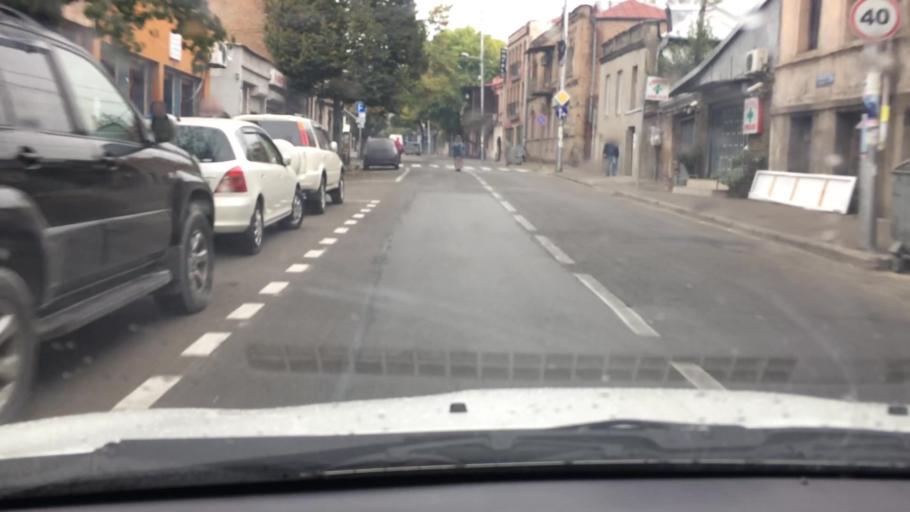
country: GE
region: T'bilisi
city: Tbilisi
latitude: 41.7068
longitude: 44.8054
